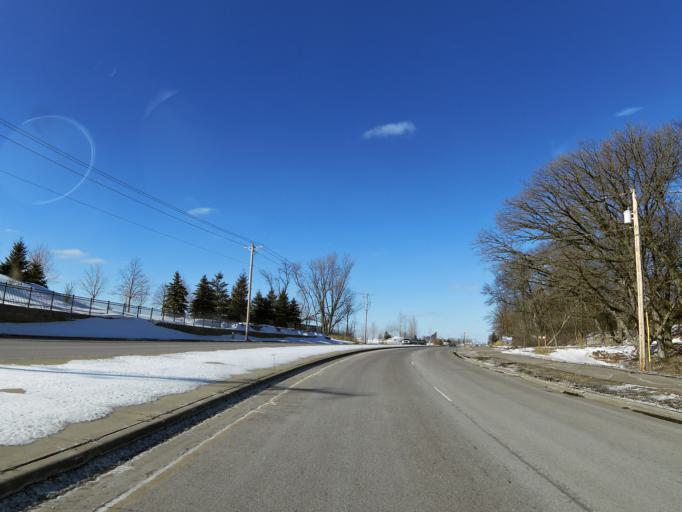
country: US
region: Minnesota
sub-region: Washington County
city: Woodbury
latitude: 44.9203
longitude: -92.9843
